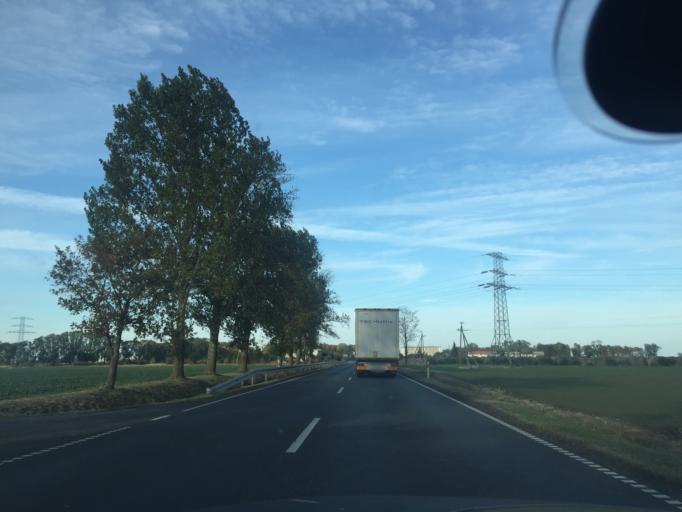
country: PL
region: Kujawsko-Pomorskie
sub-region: Powiat mogilenski
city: Strzelno
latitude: 52.6995
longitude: 18.2127
